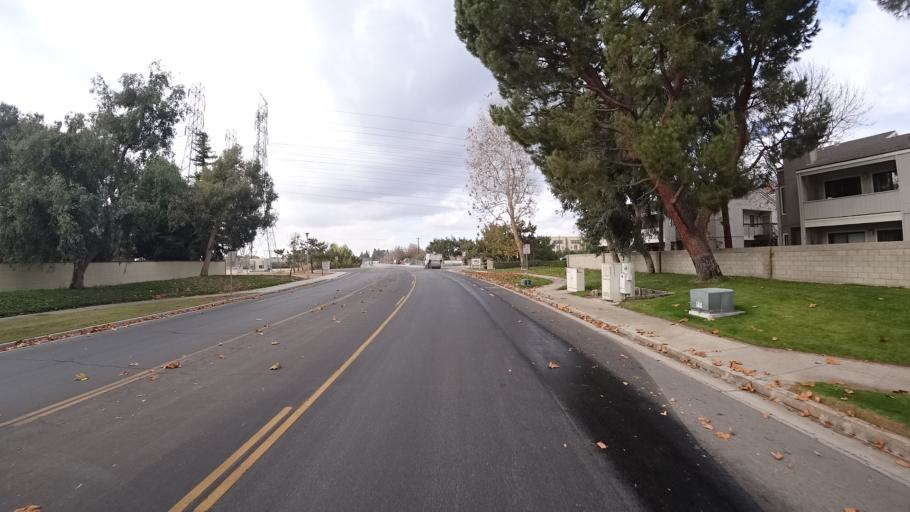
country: US
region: California
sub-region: Kern County
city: Greenacres
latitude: 35.3503
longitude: -119.0951
